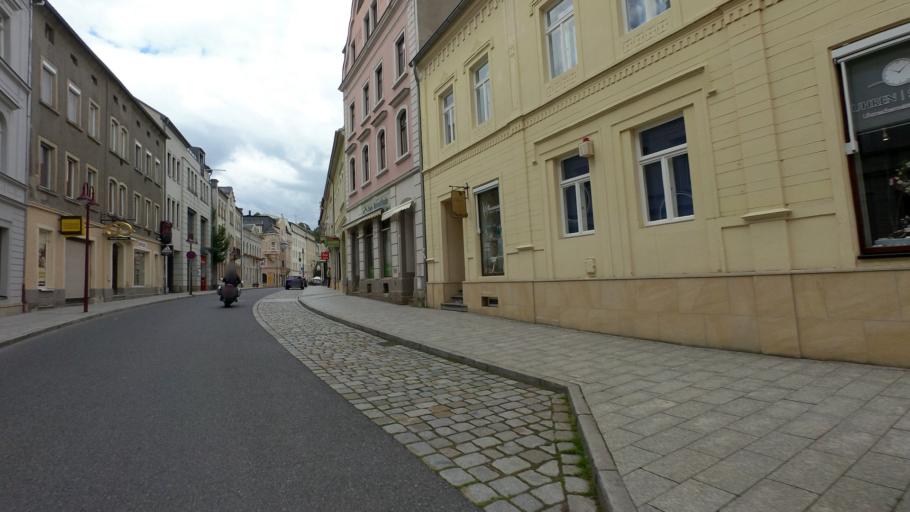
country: DE
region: Saxony
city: Sebnitz
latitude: 50.9715
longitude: 14.2707
